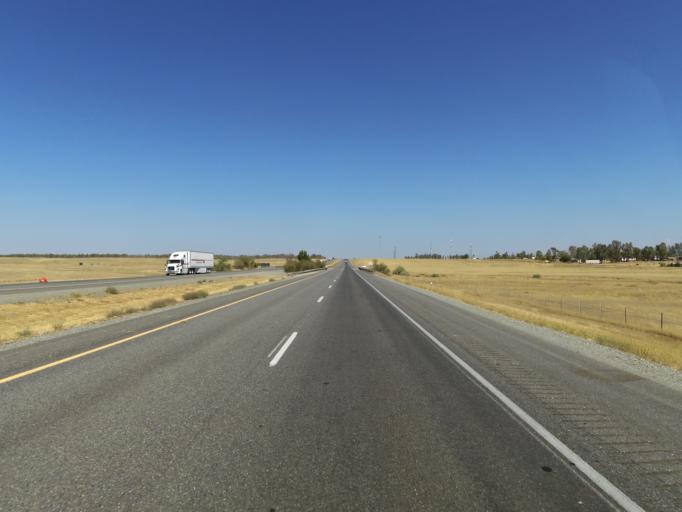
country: US
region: California
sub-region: Glenn County
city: Orland
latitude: 39.8292
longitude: -122.1998
